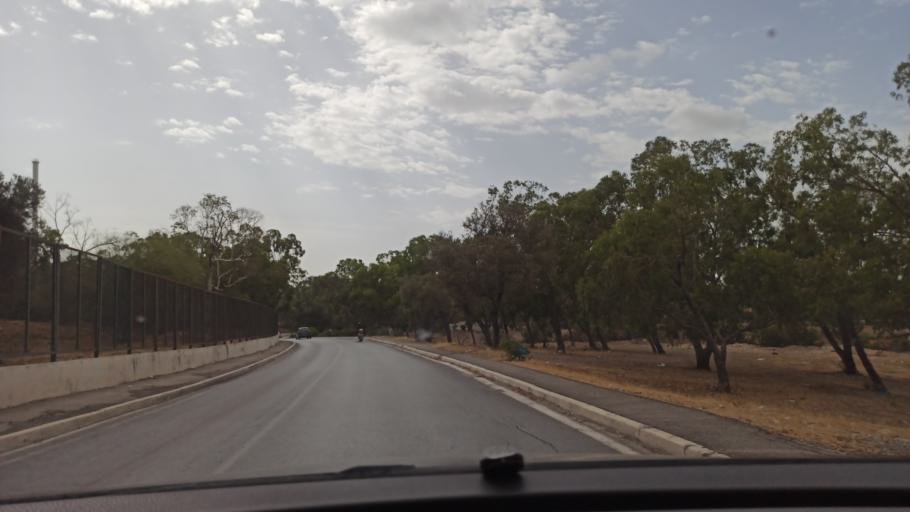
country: TN
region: Tunis
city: Tunis
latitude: 36.8265
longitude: 10.1678
